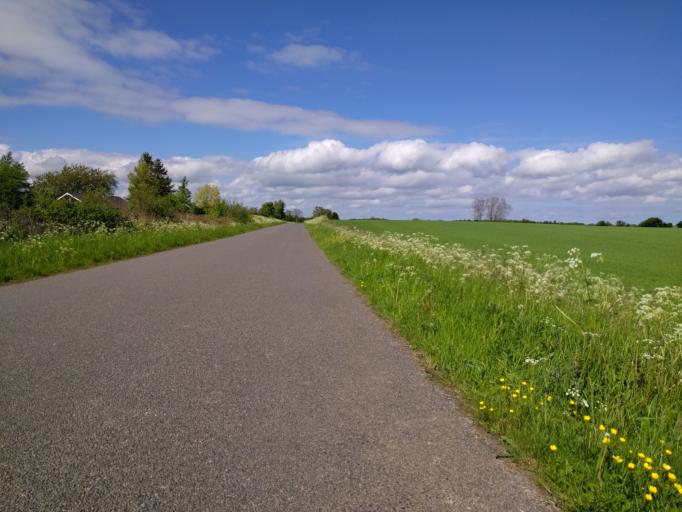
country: DK
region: Zealand
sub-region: Guldborgsund Kommune
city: Stubbekobing
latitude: 54.9175
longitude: 12.0632
